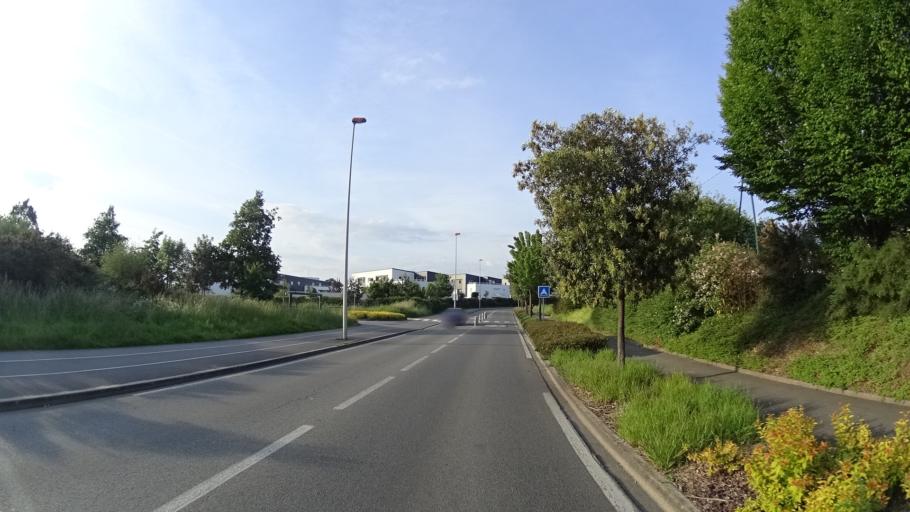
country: FR
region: Brittany
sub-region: Departement du Morbihan
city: Vannes
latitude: 47.6505
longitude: -2.7443
